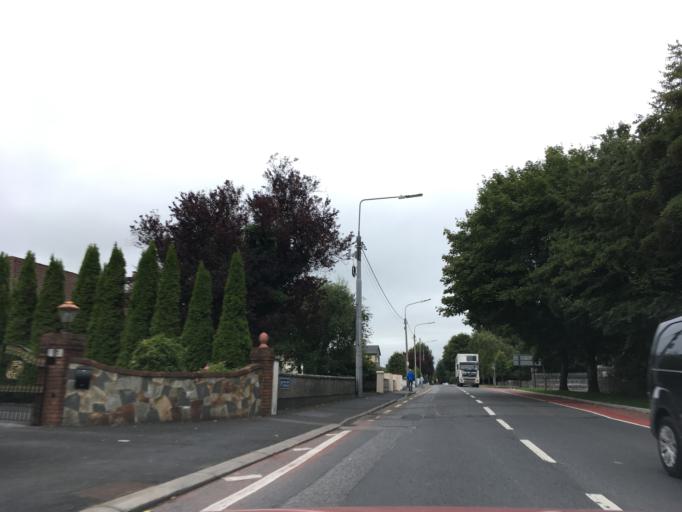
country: IE
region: Munster
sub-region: An Clar
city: Ennis
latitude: 52.8327
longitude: -8.9814
